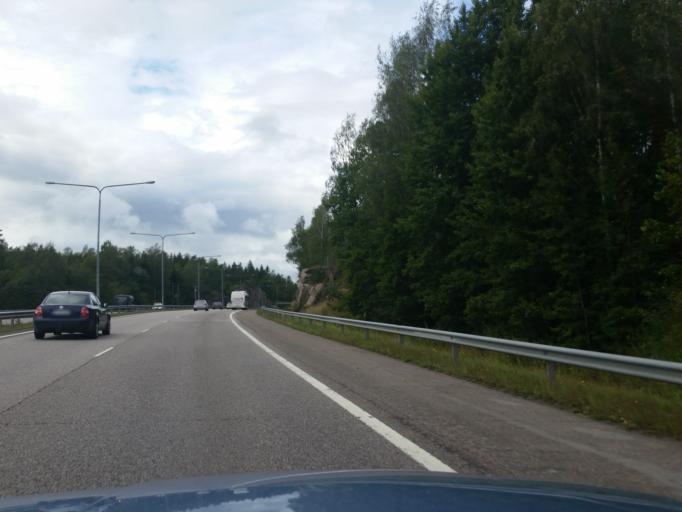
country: FI
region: Uusimaa
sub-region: Helsinki
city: Espoo
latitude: 60.2273
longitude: 24.6008
